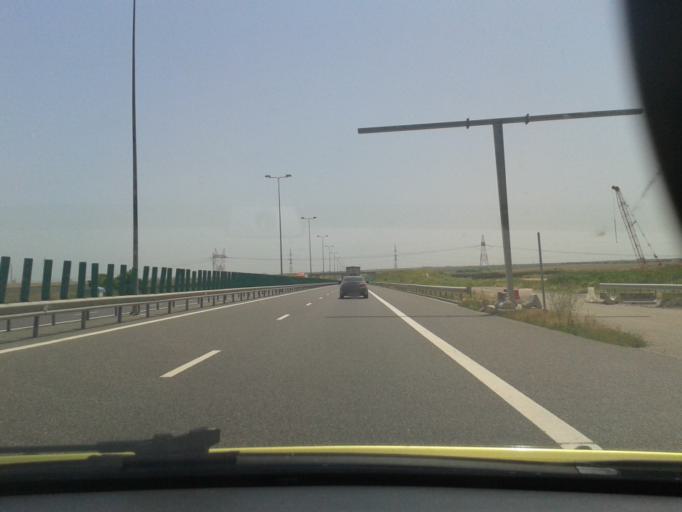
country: RO
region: Constanta
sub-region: Comuna Ovidiu
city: Ovidiu
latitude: 44.2205
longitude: 28.5514
